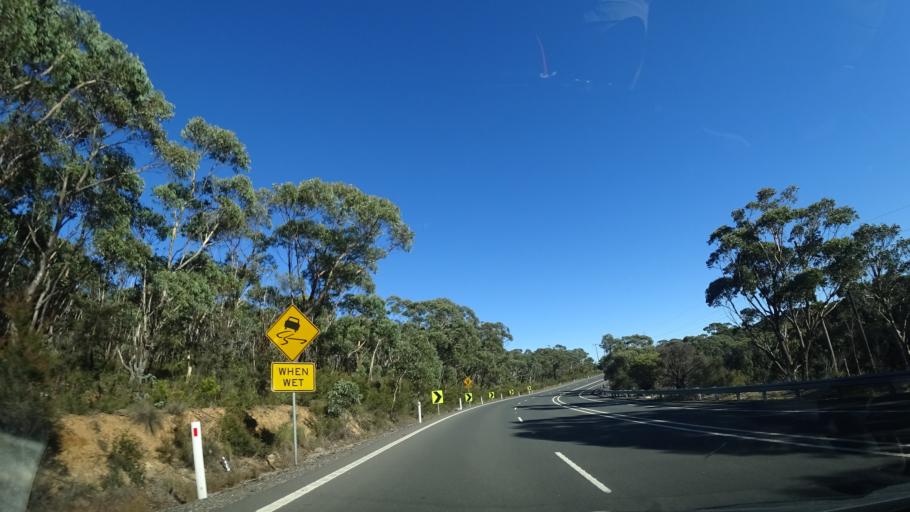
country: AU
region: New South Wales
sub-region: Blue Mountains Municipality
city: Blackheath
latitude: -33.5322
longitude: 150.3101
